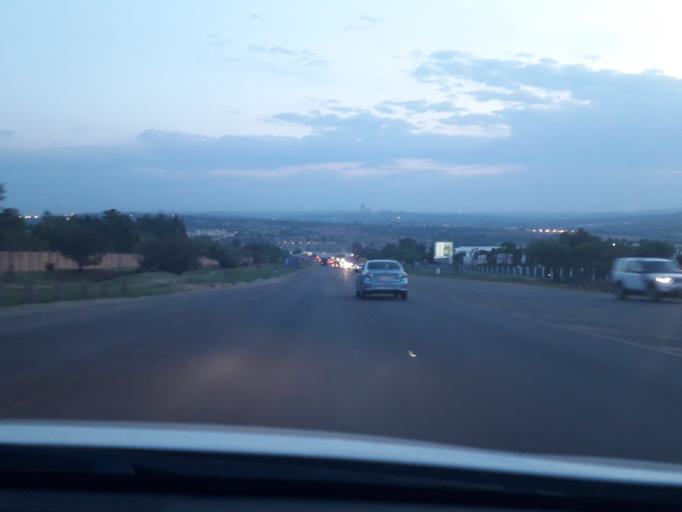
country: ZA
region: Gauteng
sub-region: City of Johannesburg Metropolitan Municipality
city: Midrand
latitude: -25.9912
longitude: 28.0768
